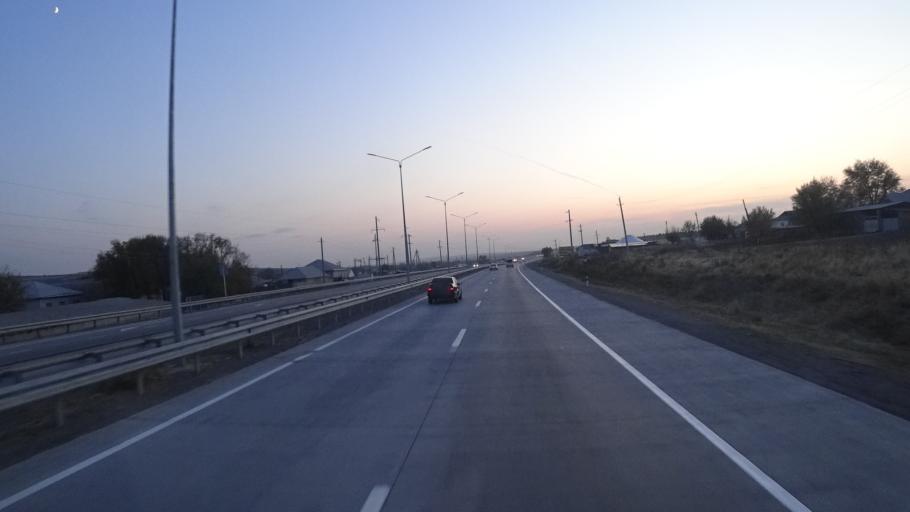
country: KZ
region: Ongtustik Qazaqstan
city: Qazyqurt
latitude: 41.8808
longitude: 69.4367
